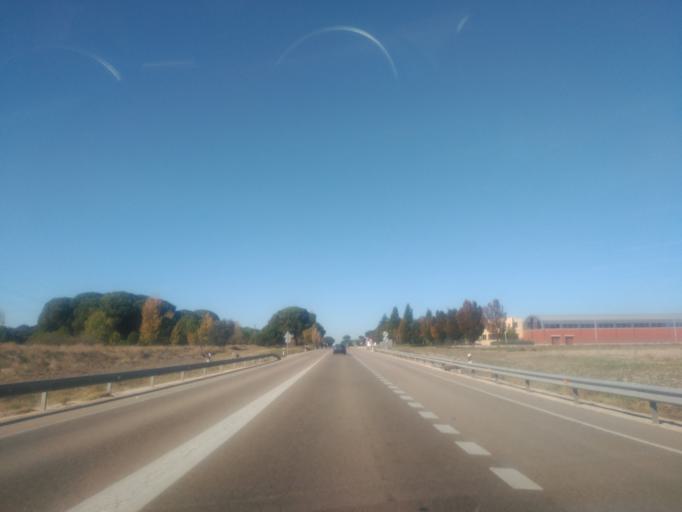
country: ES
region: Castille and Leon
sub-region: Provincia de Valladolid
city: Manzanillo
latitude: 41.6117
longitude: -4.1702
